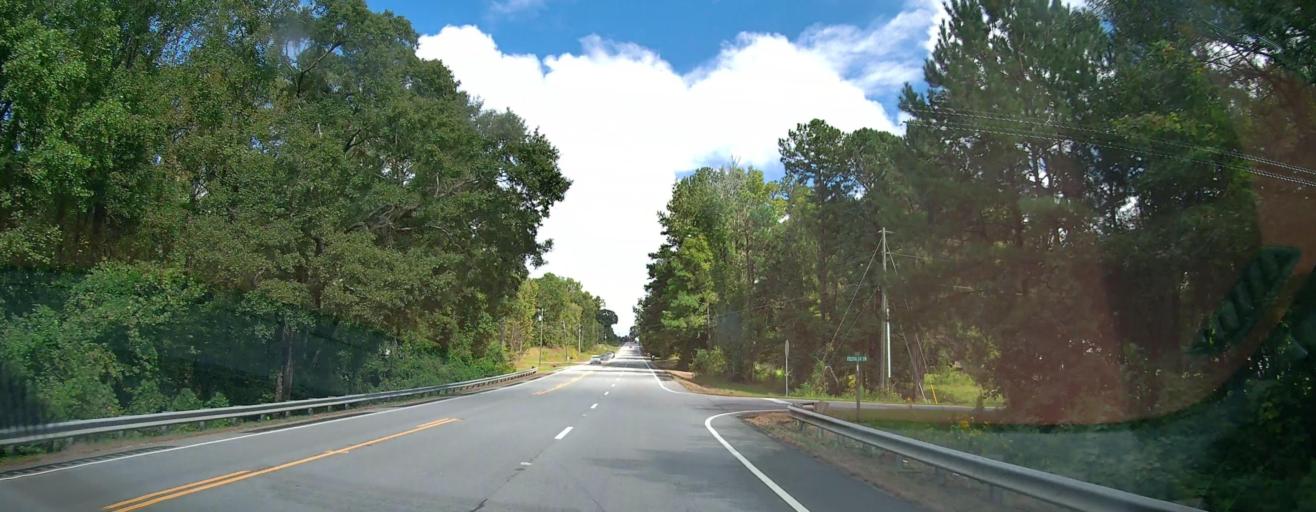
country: US
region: Georgia
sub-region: Baldwin County
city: Milledgeville
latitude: 33.0549
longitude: -83.2850
